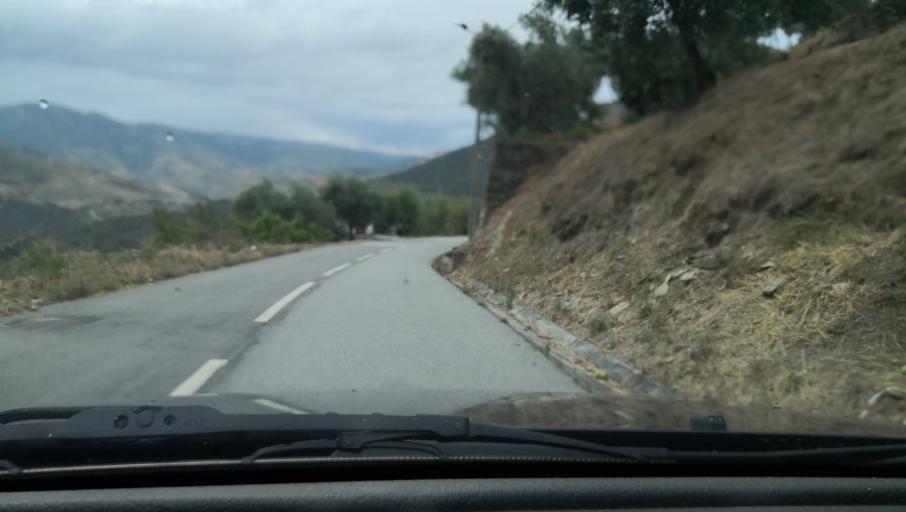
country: PT
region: Viseu
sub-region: Tabuaco
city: Tabuaco
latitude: 41.1276
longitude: -7.6273
